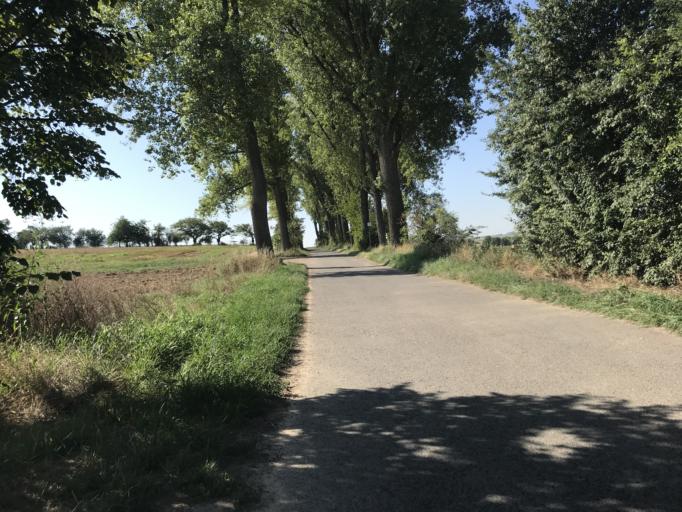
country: DE
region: Rheinland-Pfalz
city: Mainz
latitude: 49.9512
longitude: 8.2805
